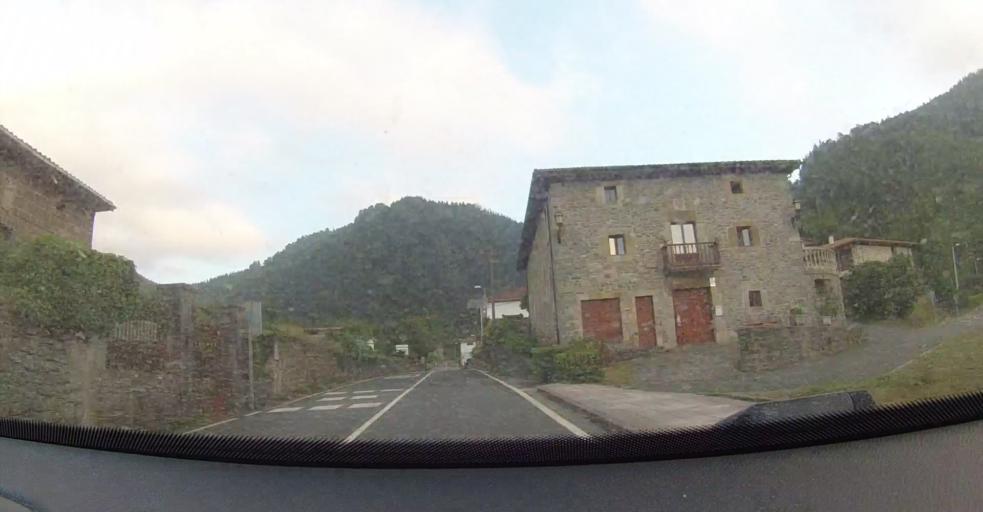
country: ES
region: Basque Country
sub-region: Bizkaia
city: Sopuerta
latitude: 43.2489
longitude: -3.1552
